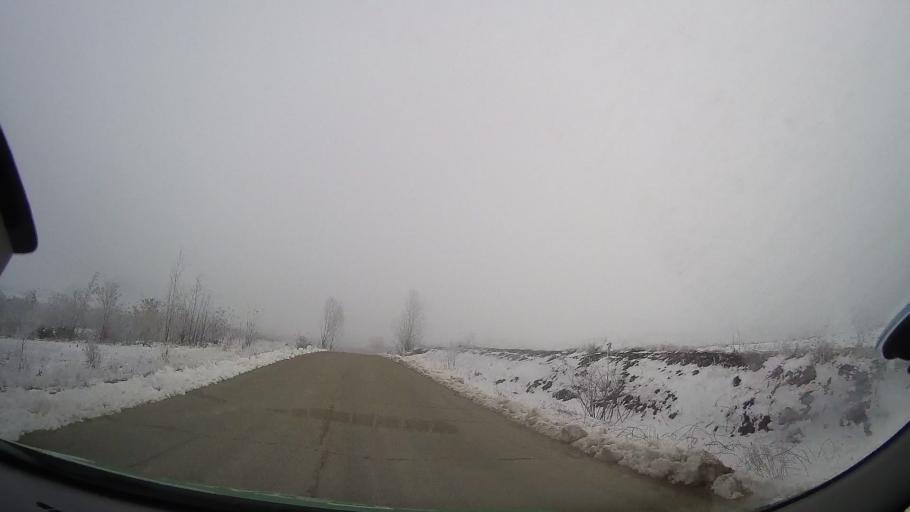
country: RO
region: Bacau
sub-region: Comuna Glavanesti
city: Frumuselu
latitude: 46.2618
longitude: 27.3276
